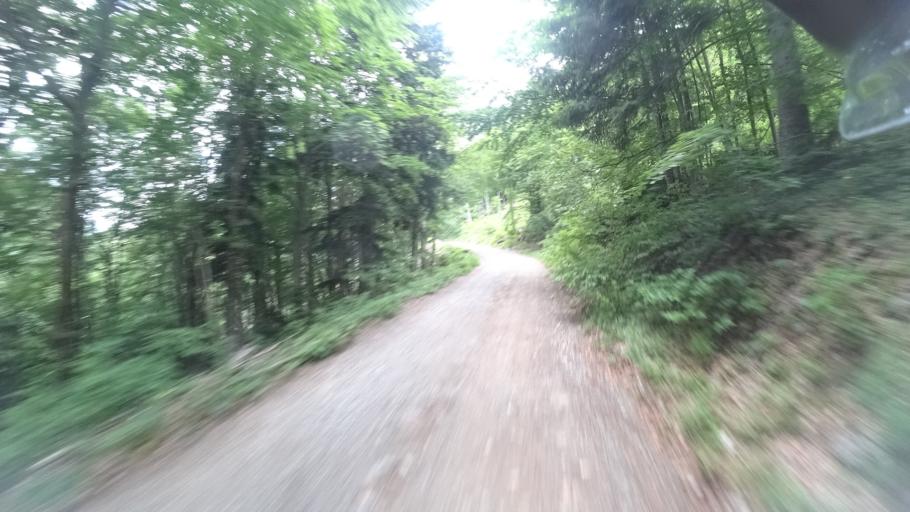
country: HR
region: Licko-Senjska
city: Gospic
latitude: 44.4680
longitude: 15.2962
